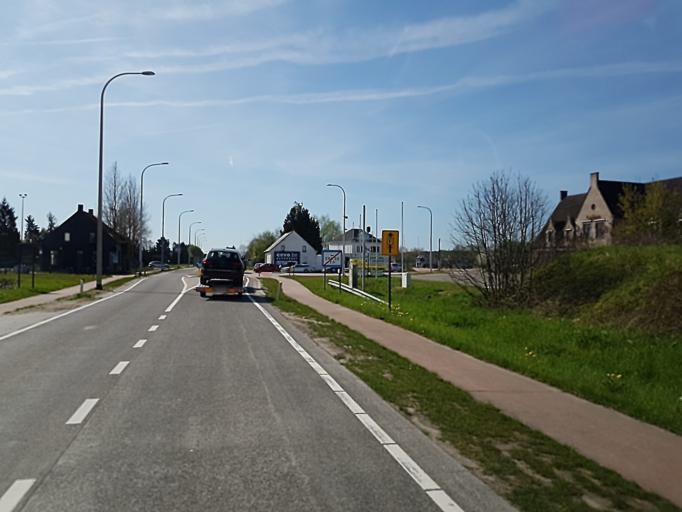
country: BE
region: Flanders
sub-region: Provincie Antwerpen
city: Westerlo
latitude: 51.1221
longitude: 4.9429
